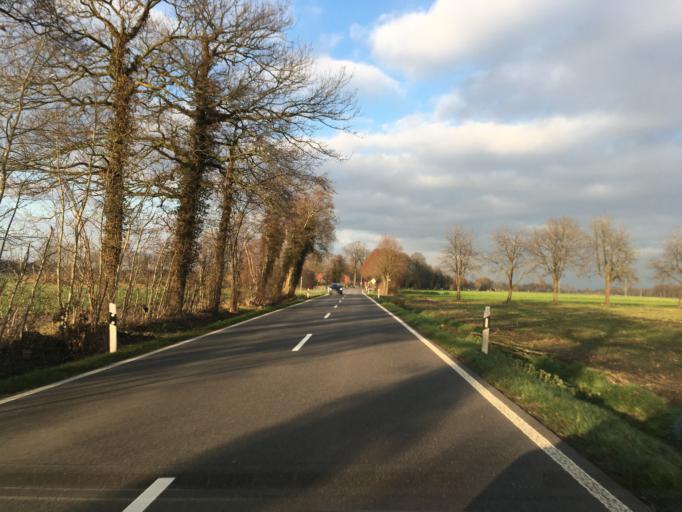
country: DE
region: North Rhine-Westphalia
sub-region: Regierungsbezirk Munster
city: Ahaus
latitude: 52.1340
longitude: 7.0067
